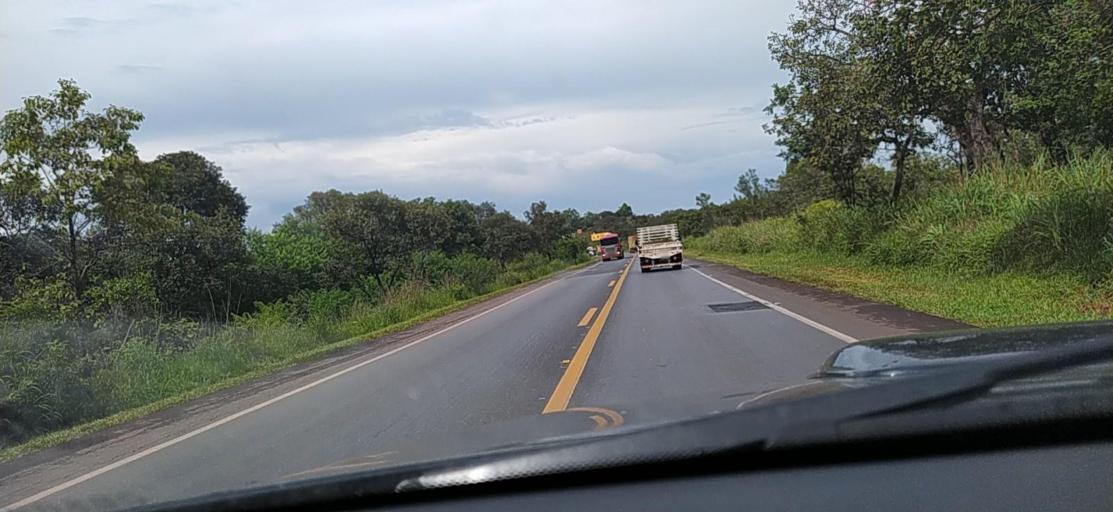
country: BR
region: Minas Gerais
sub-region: Montes Claros
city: Montes Claros
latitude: -16.8732
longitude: -43.8575
